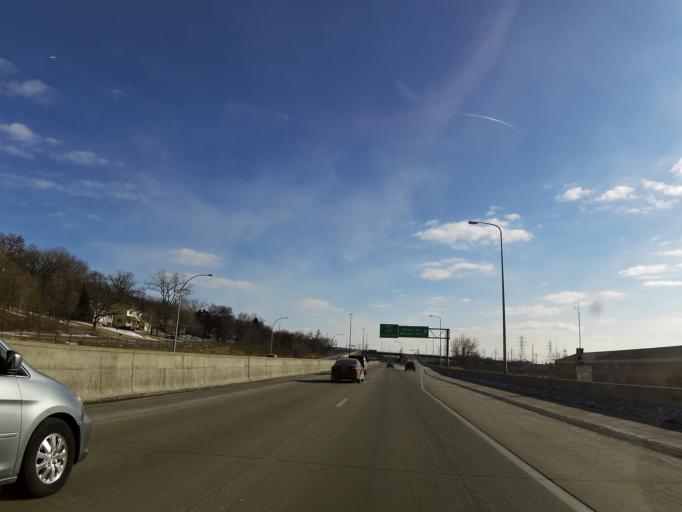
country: US
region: Minnesota
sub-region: Dakota County
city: South Saint Paul
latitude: 44.8968
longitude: -93.0091
